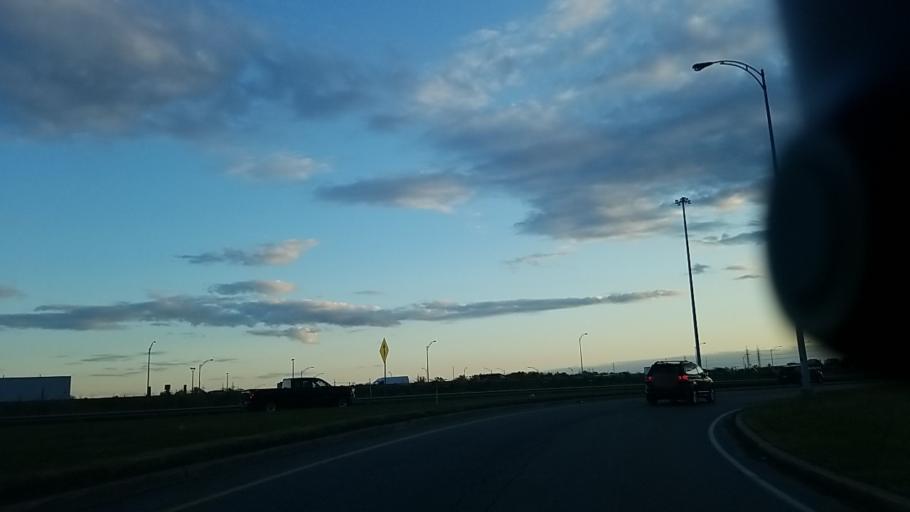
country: CA
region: Quebec
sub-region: Laval
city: Laval
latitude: 45.5866
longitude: -73.7356
